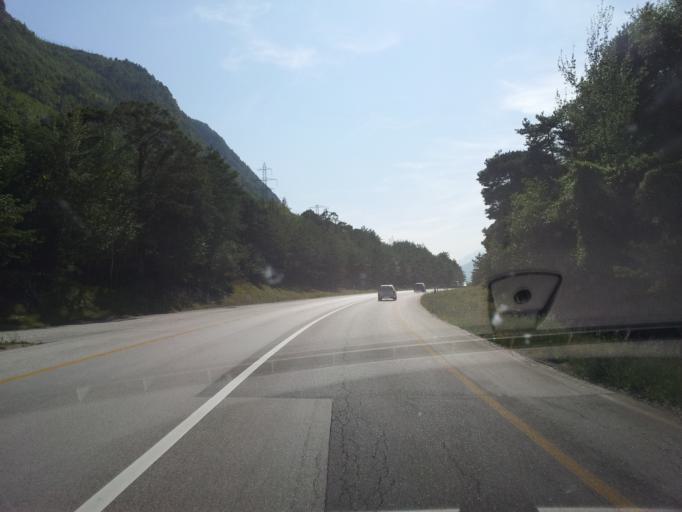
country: CH
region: Valais
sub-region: Leuk District
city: Salgesch
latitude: 46.2944
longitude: 7.5842
